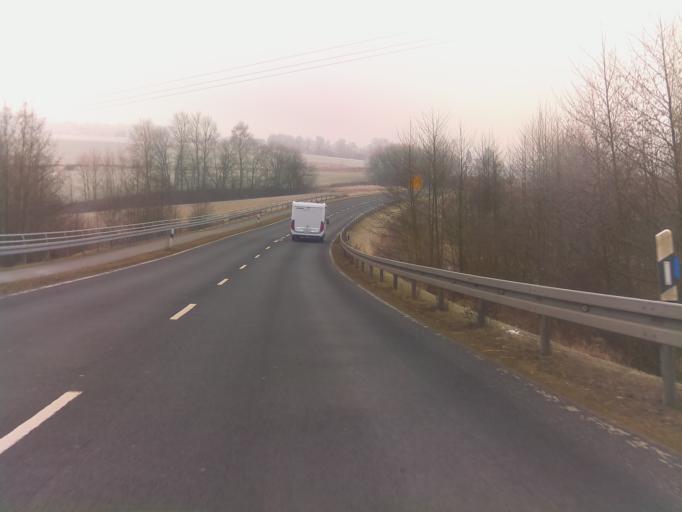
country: DE
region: Bavaria
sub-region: Regierungsbezirk Unterfranken
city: Blankenbach
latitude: 50.0747
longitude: 9.2409
